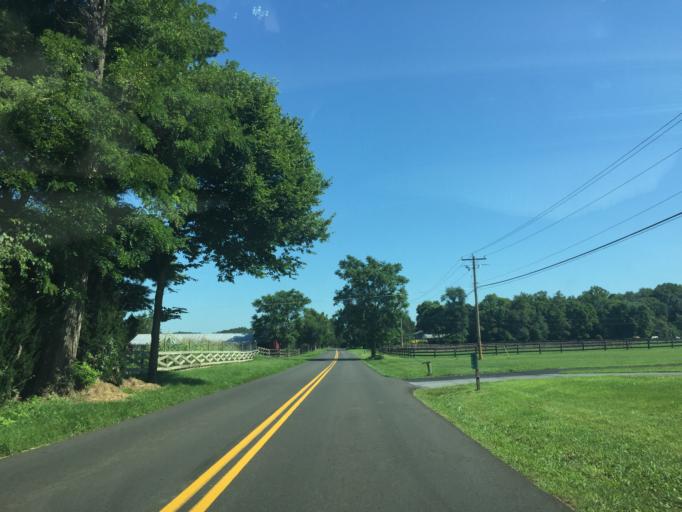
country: US
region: Virginia
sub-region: Warren County
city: Apple Mountain Lake
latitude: 38.9473
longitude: -78.1247
